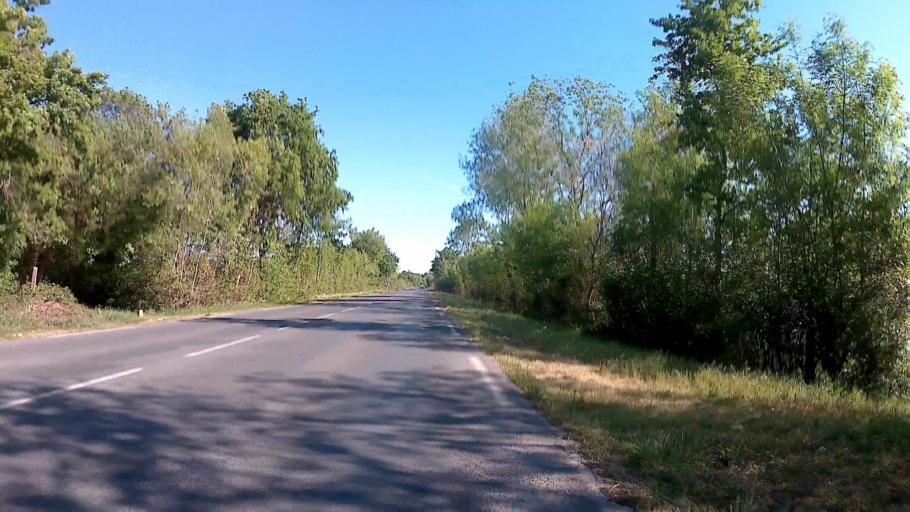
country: FR
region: Aquitaine
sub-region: Departement de la Gironde
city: Cadaujac
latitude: 44.7656
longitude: -0.5287
